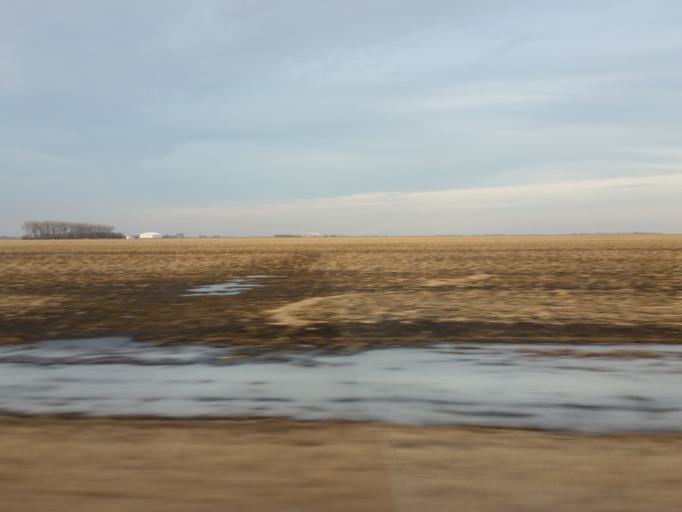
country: US
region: North Dakota
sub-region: Traill County
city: Mayville
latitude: 47.4151
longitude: -97.3261
